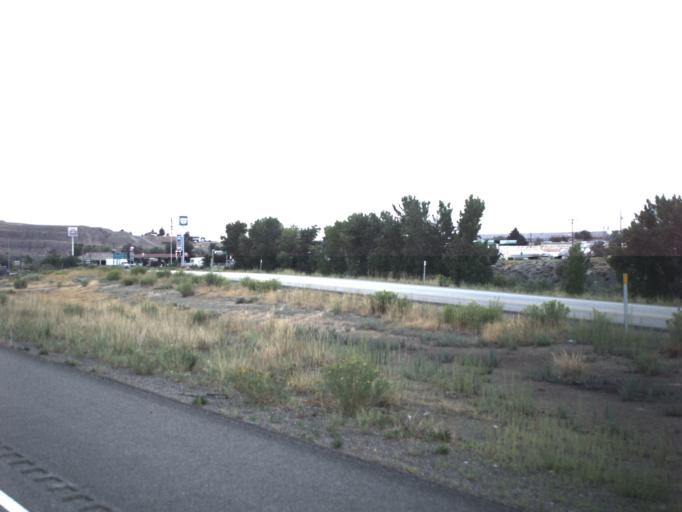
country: US
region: Utah
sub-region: Carbon County
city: Price
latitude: 39.5891
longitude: -110.8151
